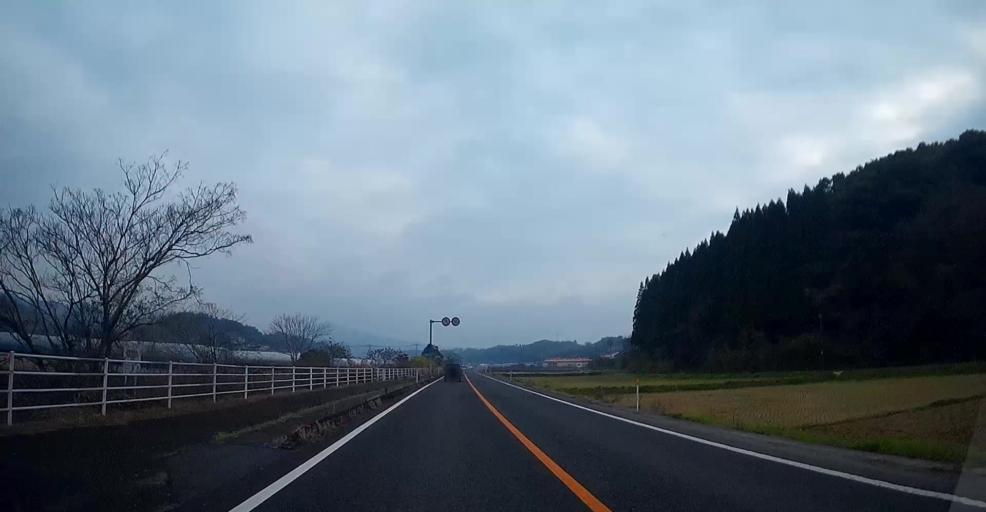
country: JP
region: Kumamoto
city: Yatsushiro
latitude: 32.6251
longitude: 130.5239
